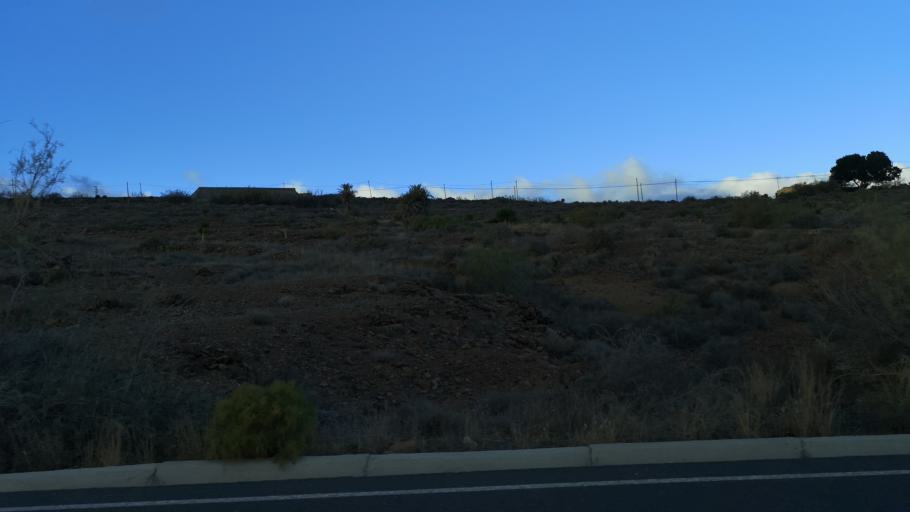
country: ES
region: Canary Islands
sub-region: Provincia de Santa Cruz de Tenerife
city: Alajero
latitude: 28.0373
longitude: -17.2214
